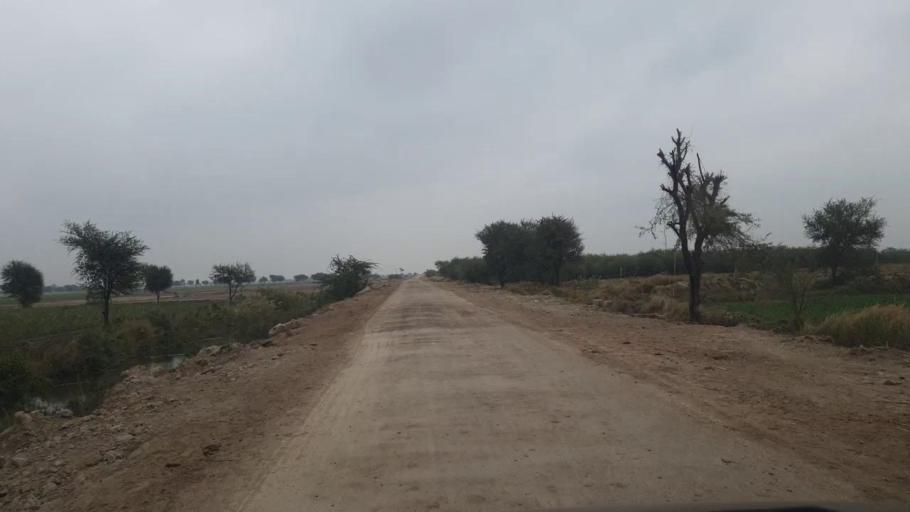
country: PK
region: Sindh
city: Shahdadpur
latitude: 25.9083
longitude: 68.7055
